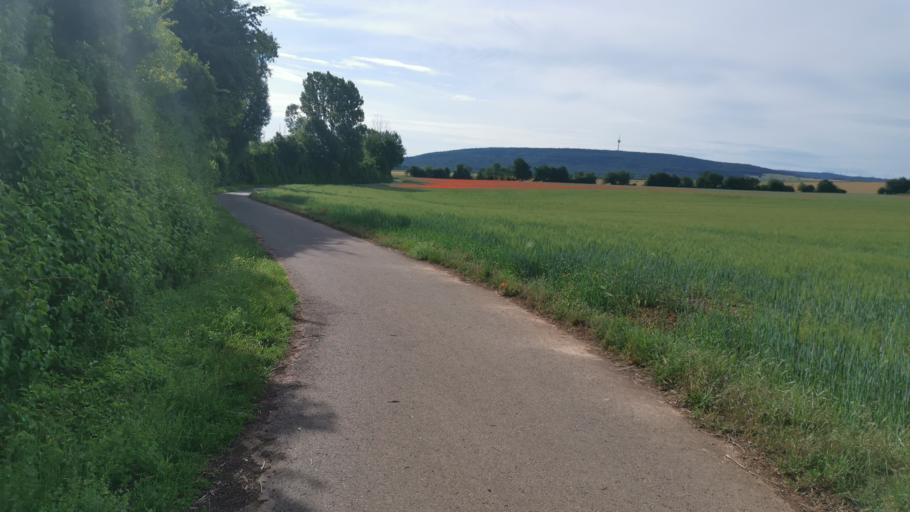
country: DE
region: Rheinland-Pfalz
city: Mandel
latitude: 49.8565
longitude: 7.7860
